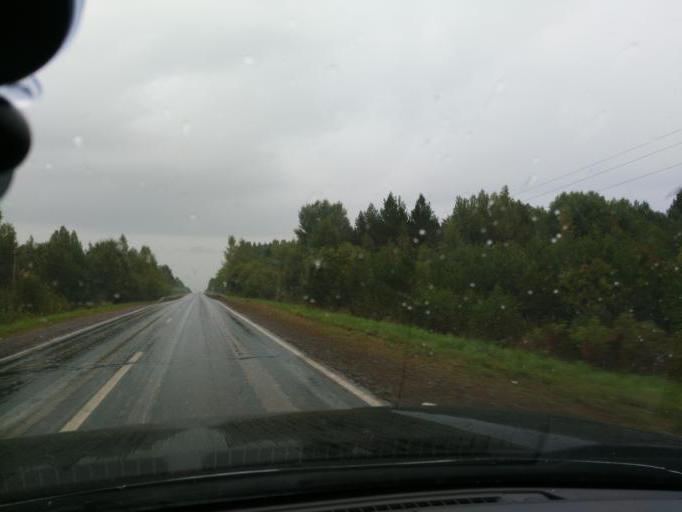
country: RU
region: Perm
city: Osa
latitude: 57.1217
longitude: 55.5236
